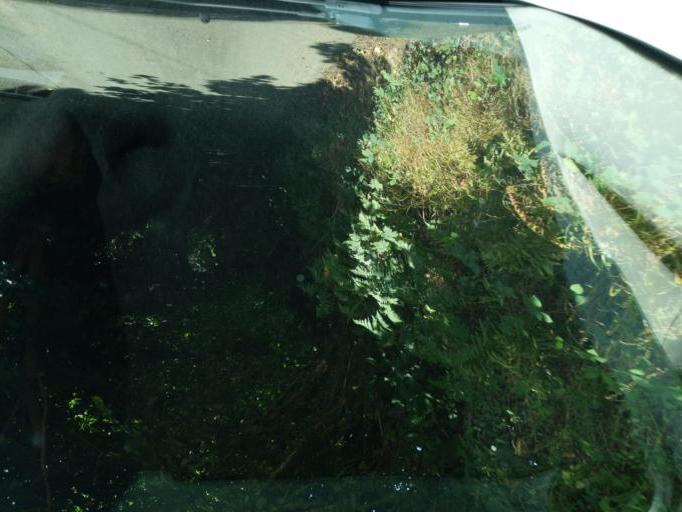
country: GB
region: England
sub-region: Devon
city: Modbury
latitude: 50.3672
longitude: -3.9036
